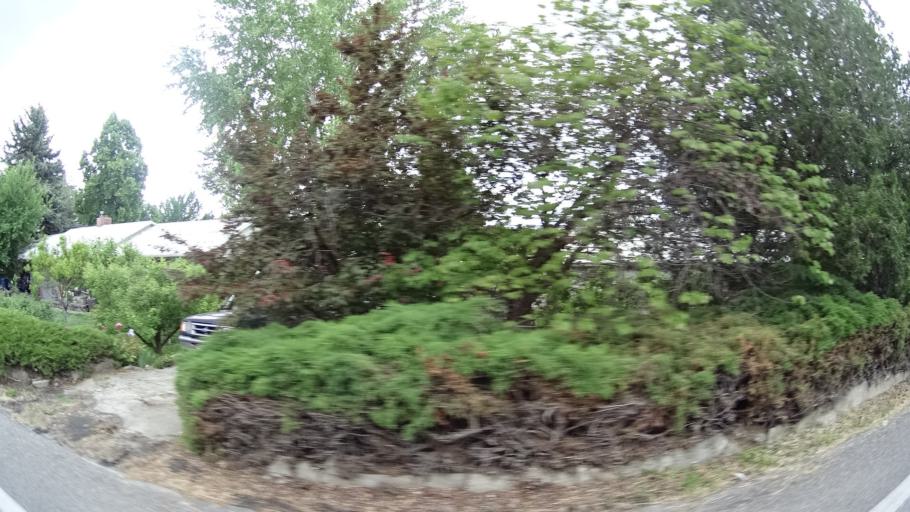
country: US
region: Idaho
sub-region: Ada County
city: Garden City
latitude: 43.6689
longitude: -116.2538
